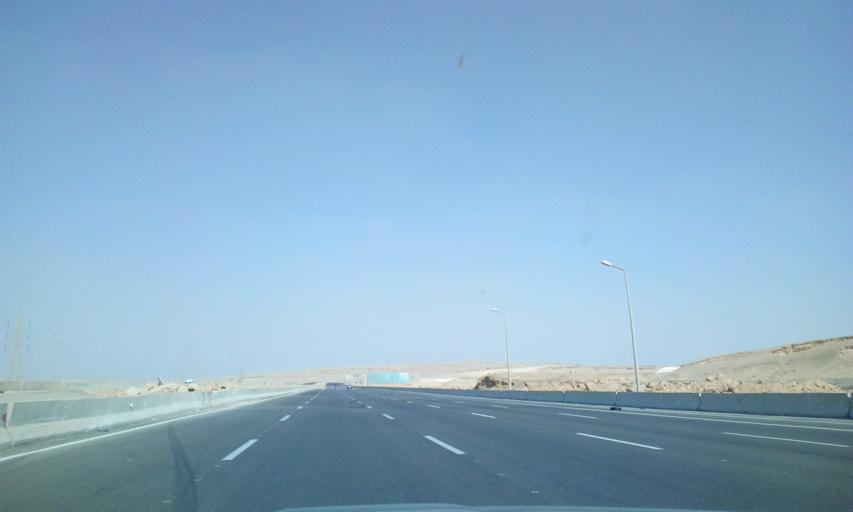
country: EG
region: As Suways
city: Ain Sukhna
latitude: 29.7606
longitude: 31.9848
